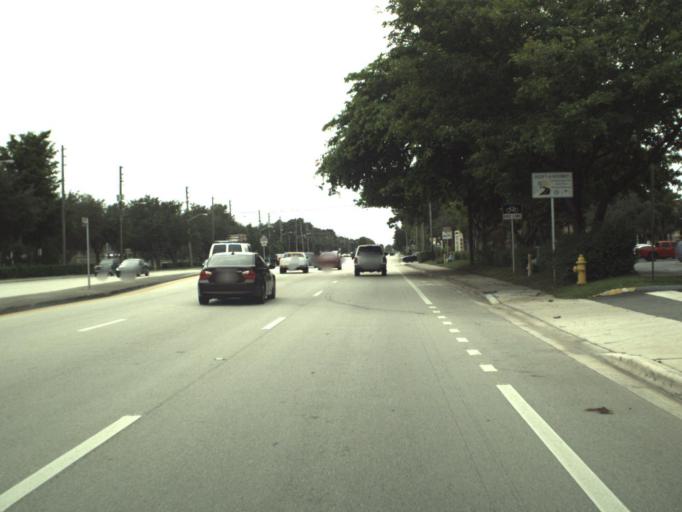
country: US
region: Florida
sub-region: Palm Beach County
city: North Palm Beach
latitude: 26.8085
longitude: -80.1065
